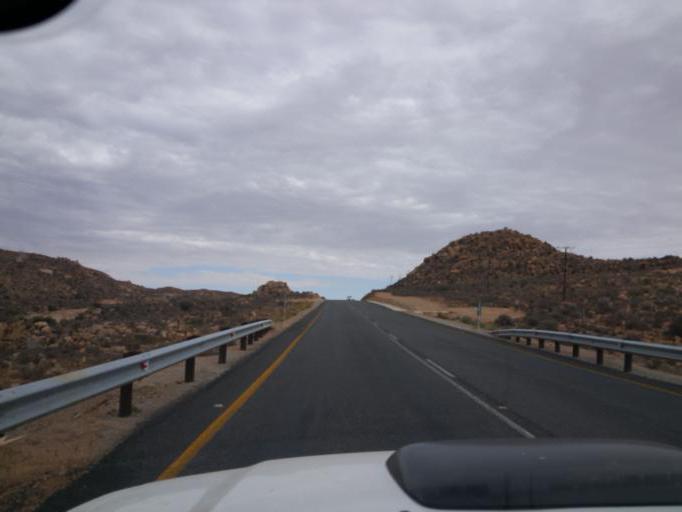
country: ZA
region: Northern Cape
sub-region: Namakwa District Municipality
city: Springbok
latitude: -29.4388
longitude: 17.8345
